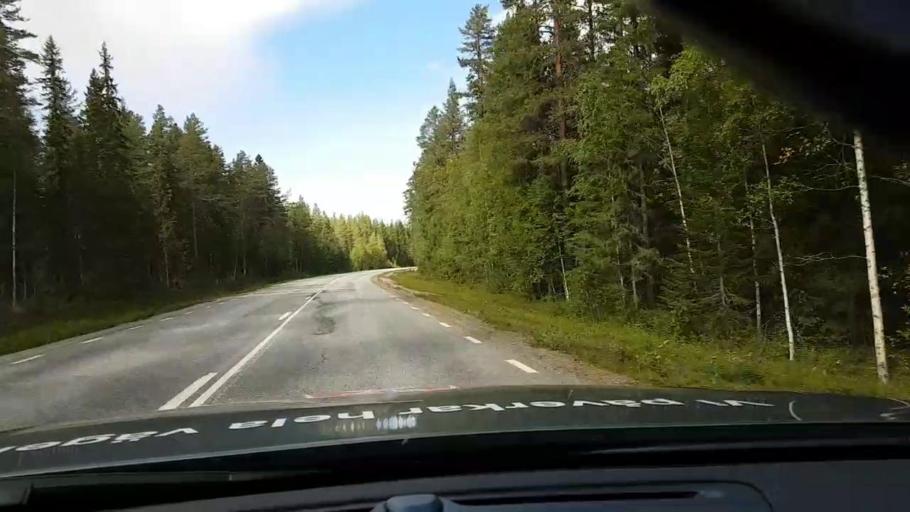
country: SE
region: Vaesternorrland
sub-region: OErnskoeldsviks Kommun
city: Bredbyn
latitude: 63.6039
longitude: 17.9035
